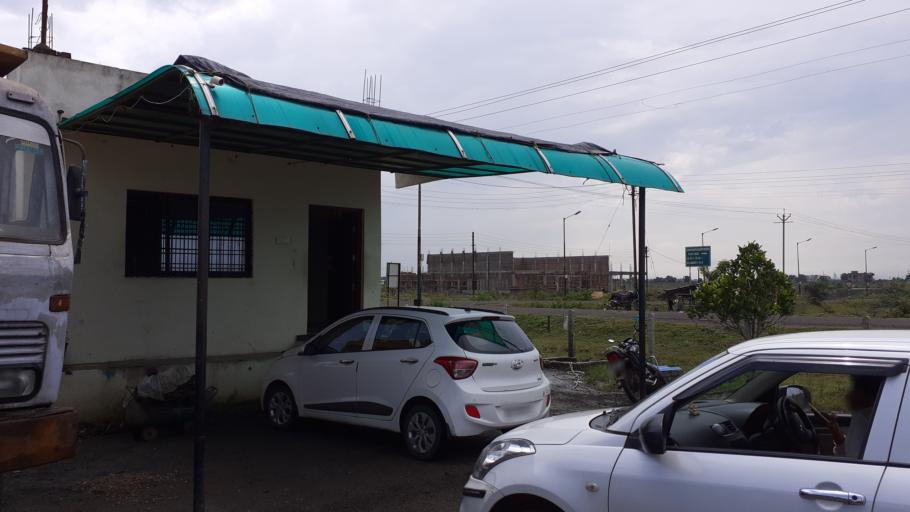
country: IN
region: Maharashtra
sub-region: Chandrapur
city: Chandrapur
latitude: 19.9727
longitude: 79.2296
